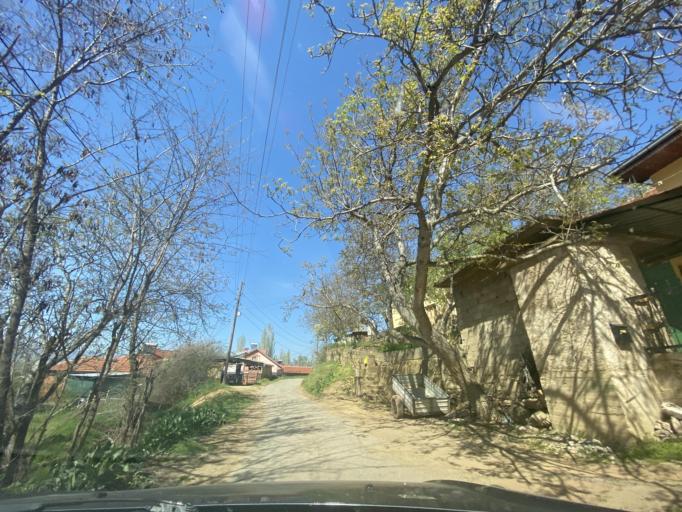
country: MK
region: Zrnovci
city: Zrnovci
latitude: 41.8552
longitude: 22.4484
